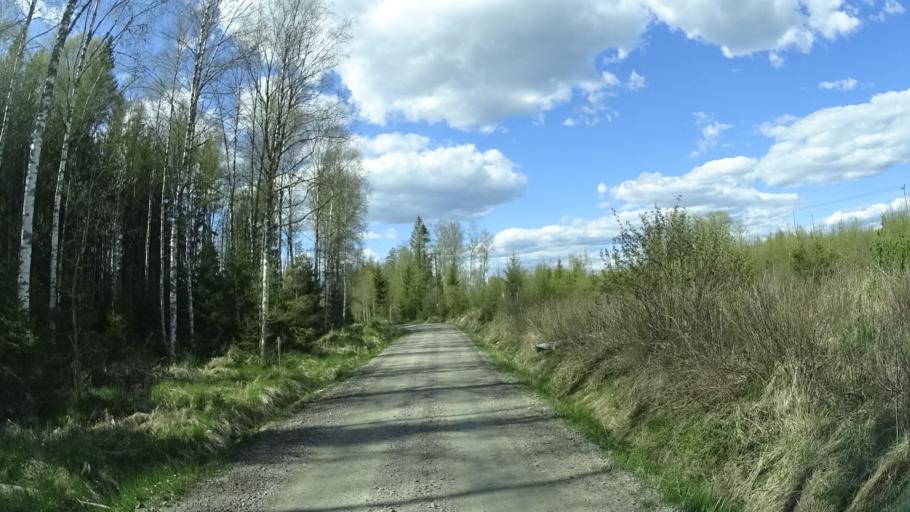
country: SE
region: OErebro
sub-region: Orebro Kommun
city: Garphyttan
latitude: 59.4156
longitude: 14.8742
